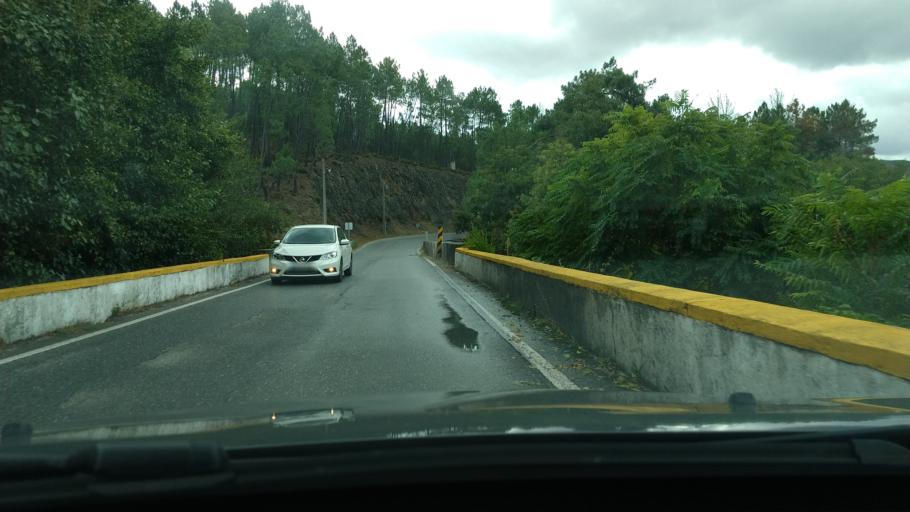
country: PT
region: Castelo Branco
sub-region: Covilha
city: Covilha
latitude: 40.2410
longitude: -7.5910
